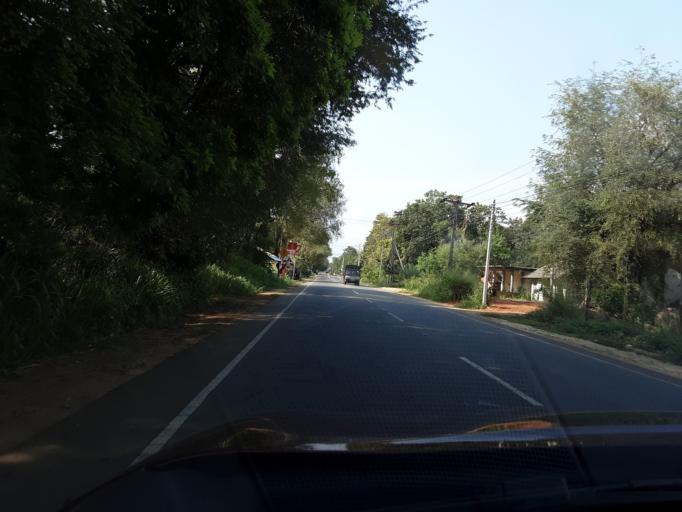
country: LK
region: Uva
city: Haputale
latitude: 6.5810
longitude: 81.1404
